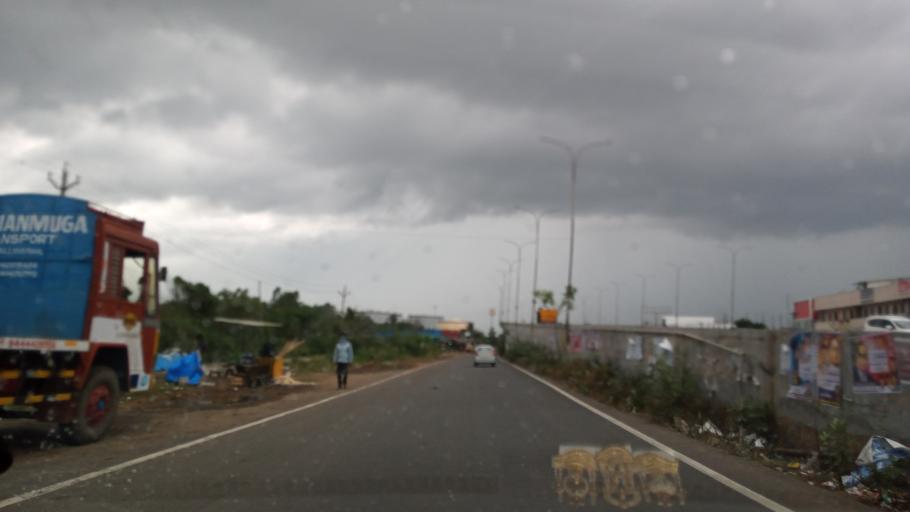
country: IN
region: Tamil Nadu
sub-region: Kancheepuram
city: Madambakkam
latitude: 12.8502
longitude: 79.9408
